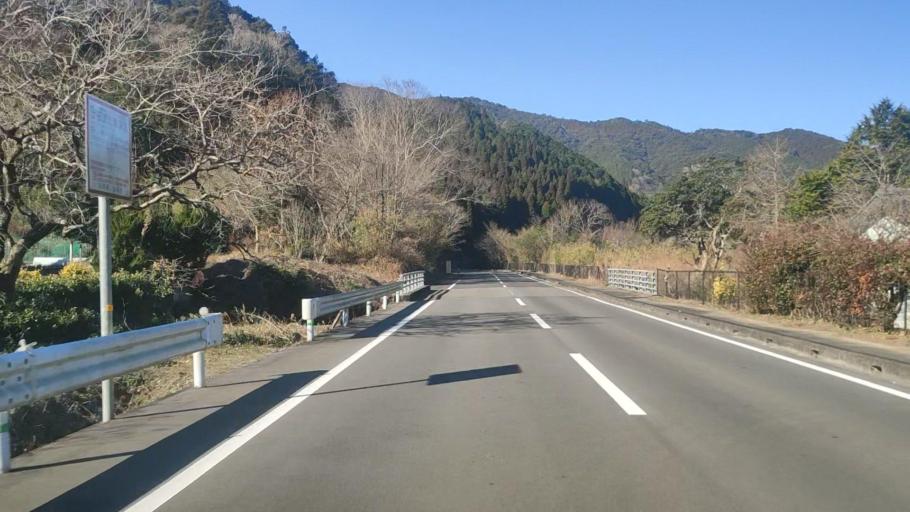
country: JP
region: Miyazaki
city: Nobeoka
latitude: 32.7472
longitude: 131.8079
